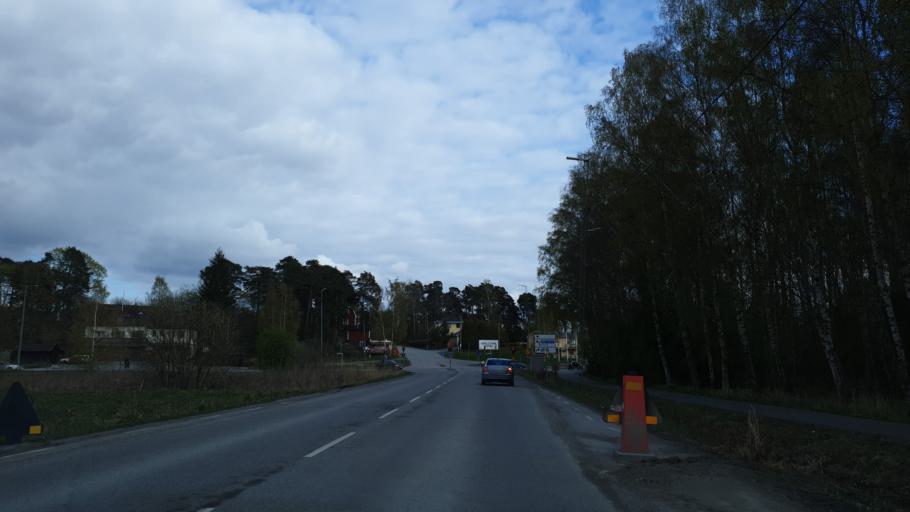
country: SE
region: Stockholm
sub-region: Jarfalla Kommun
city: Jakobsberg
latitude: 59.4073
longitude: 17.8675
